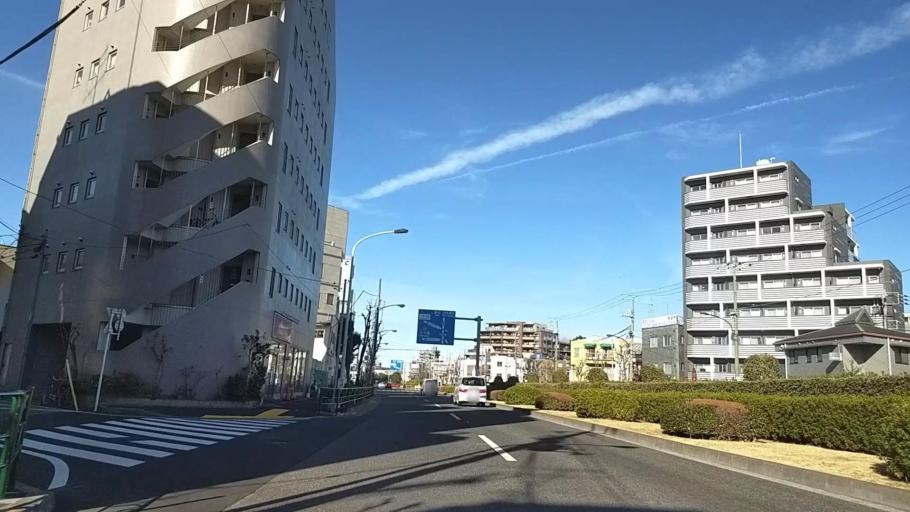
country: JP
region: Kanagawa
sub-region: Kawasaki-shi
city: Kawasaki
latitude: 35.5707
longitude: 139.6893
